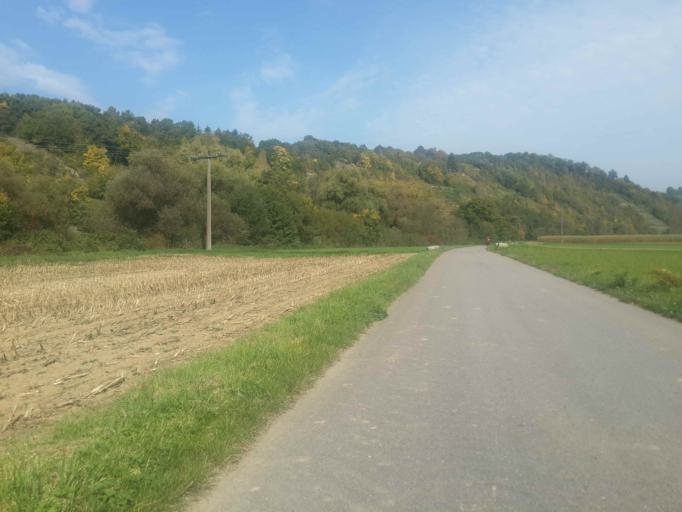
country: DE
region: Baden-Wuerttemberg
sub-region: Regierungsbezirk Stuttgart
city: Neudenau
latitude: 49.2966
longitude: 9.2991
